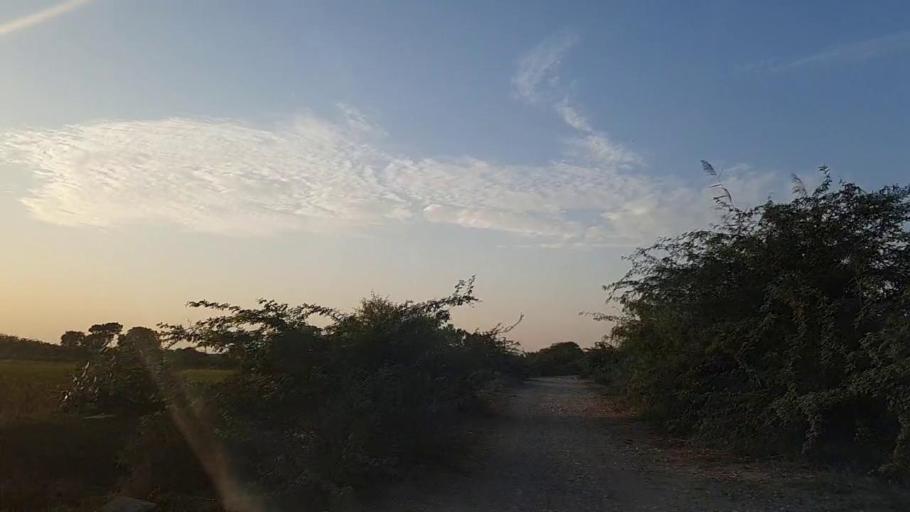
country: PK
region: Sindh
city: Chuhar Jamali
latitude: 24.4487
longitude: 68.1181
